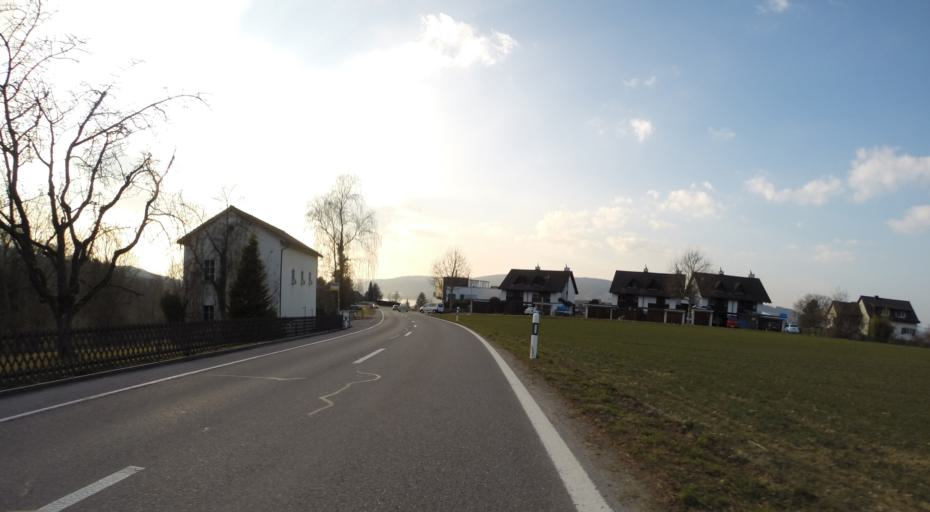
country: CH
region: Thurgau
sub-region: Frauenfeld District
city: Steckborn
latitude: 47.6596
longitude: 8.9870
